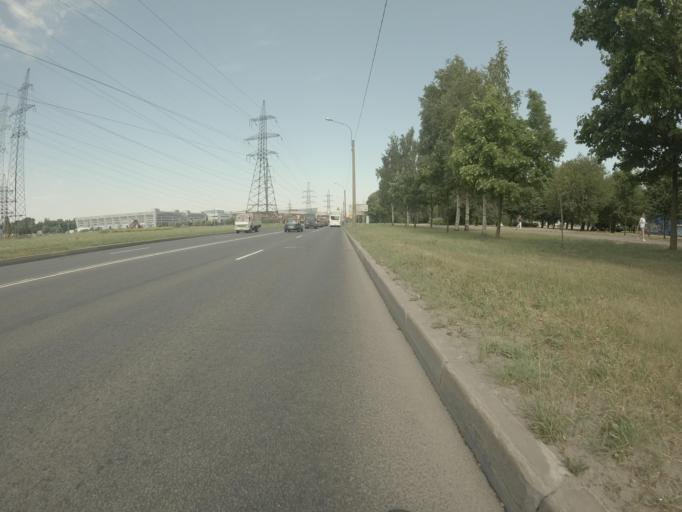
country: RU
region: St.-Petersburg
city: Krasnogvargeisky
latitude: 59.9434
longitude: 30.4638
